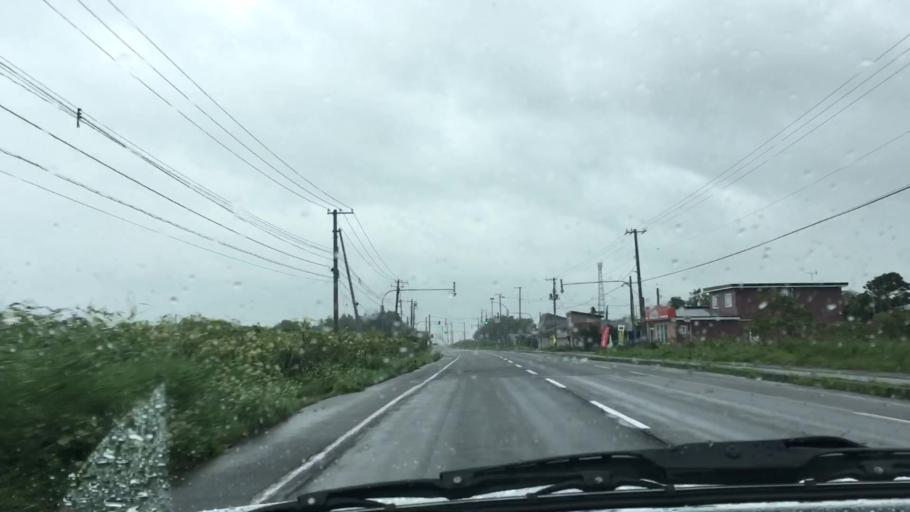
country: JP
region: Hokkaido
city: Nanae
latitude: 42.3160
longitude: 140.2742
